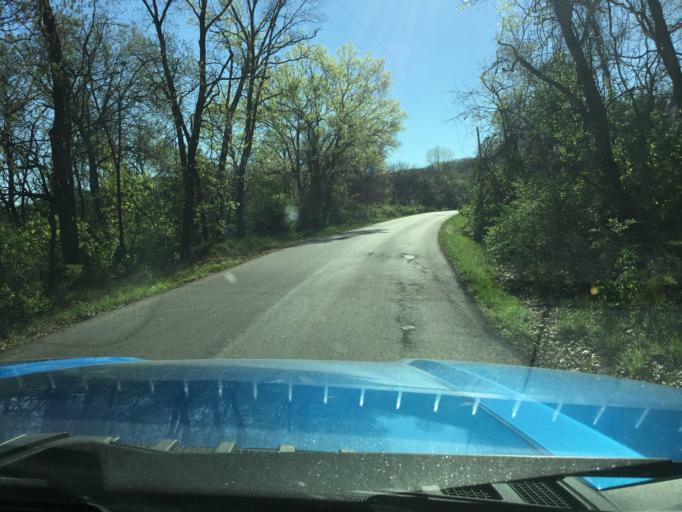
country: US
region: Kansas
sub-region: Douglas County
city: Lawrence
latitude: 38.9933
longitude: -95.3026
